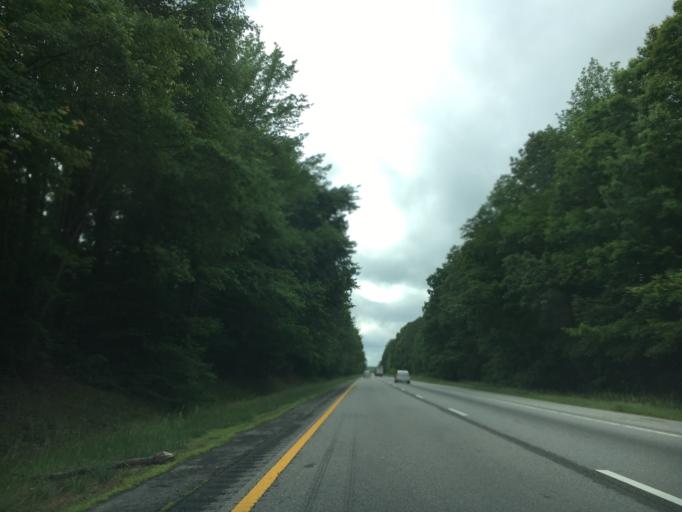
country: US
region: Virginia
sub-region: Mecklenburg County
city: South Hill
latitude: 36.7712
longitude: -78.0486
